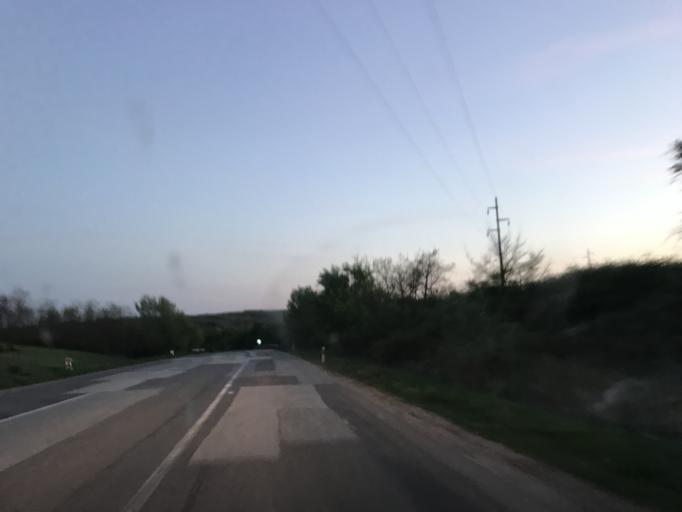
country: RS
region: Central Serbia
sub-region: Zajecarski Okrug
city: Zajecar
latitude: 43.9577
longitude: 22.2988
